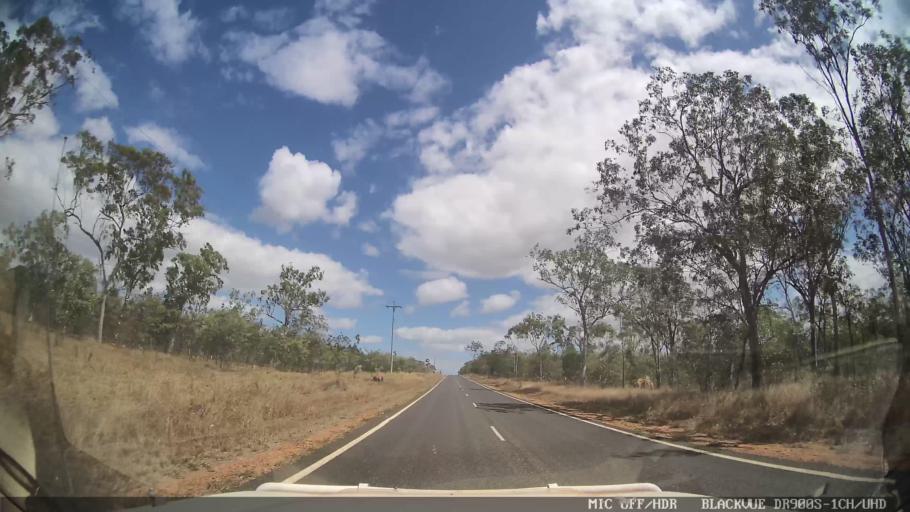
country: AU
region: Queensland
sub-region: Tablelands
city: Ravenshoe
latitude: -17.7282
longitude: 145.0465
